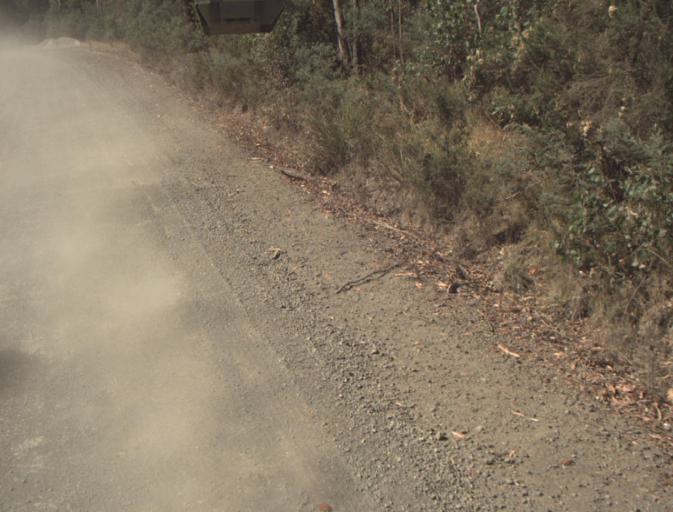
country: AU
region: Tasmania
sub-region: Launceston
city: Newstead
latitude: -41.3690
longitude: 147.2387
